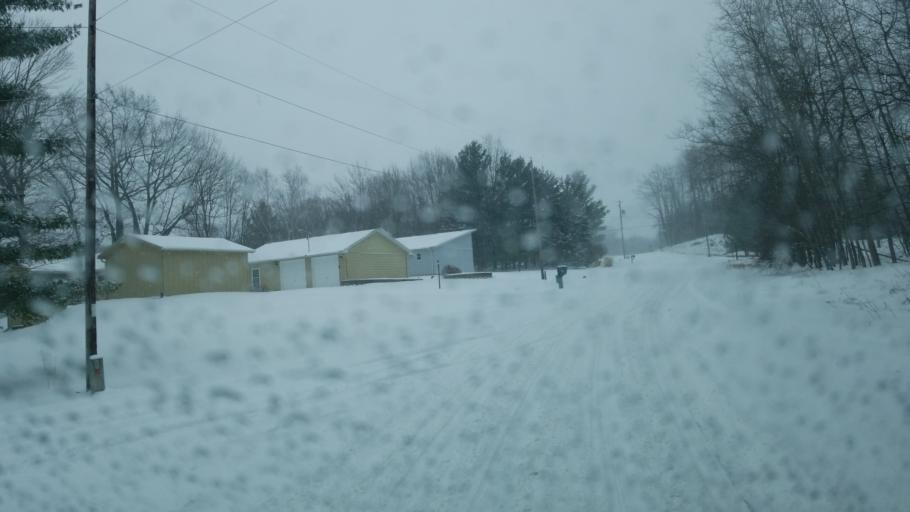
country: US
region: Michigan
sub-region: Mecosta County
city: Canadian Lakes
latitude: 43.6046
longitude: -85.3037
